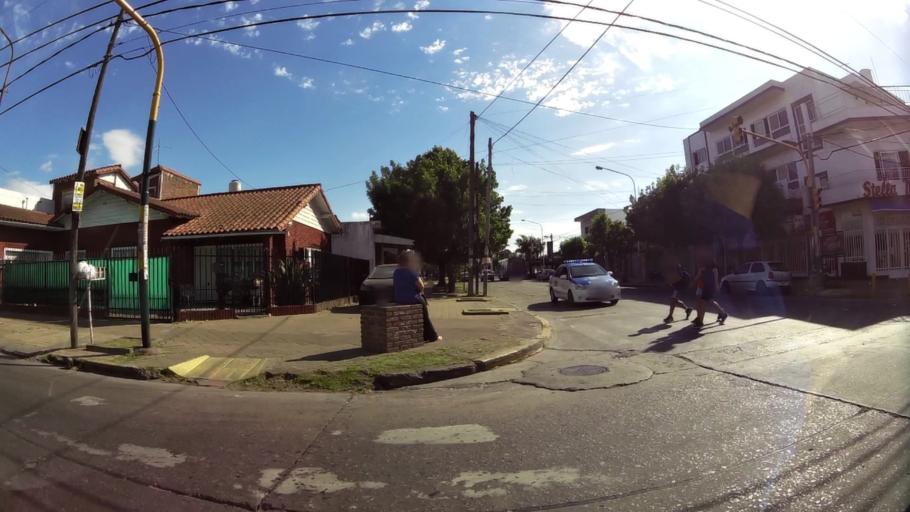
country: AR
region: Buenos Aires
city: San Justo
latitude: -34.6628
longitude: -58.5816
